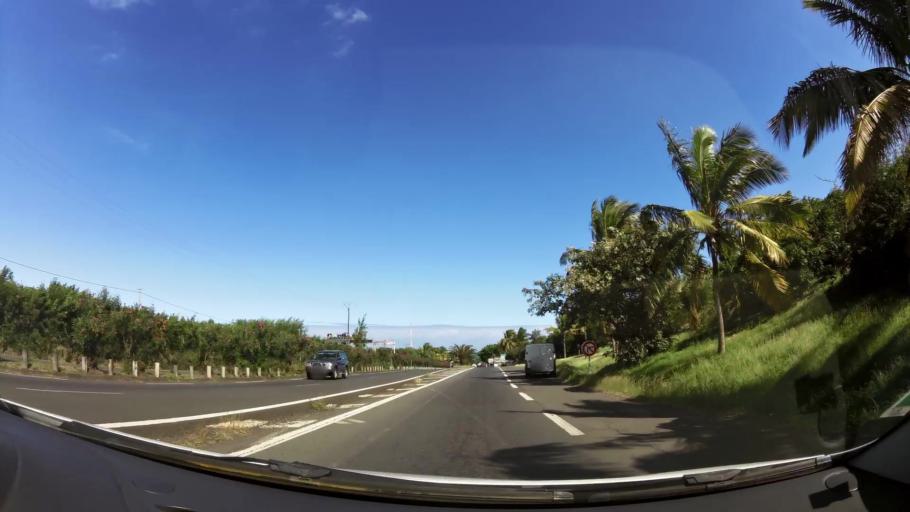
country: RE
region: Reunion
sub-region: Reunion
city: Saint-Pierre
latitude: -21.3225
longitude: 55.4879
